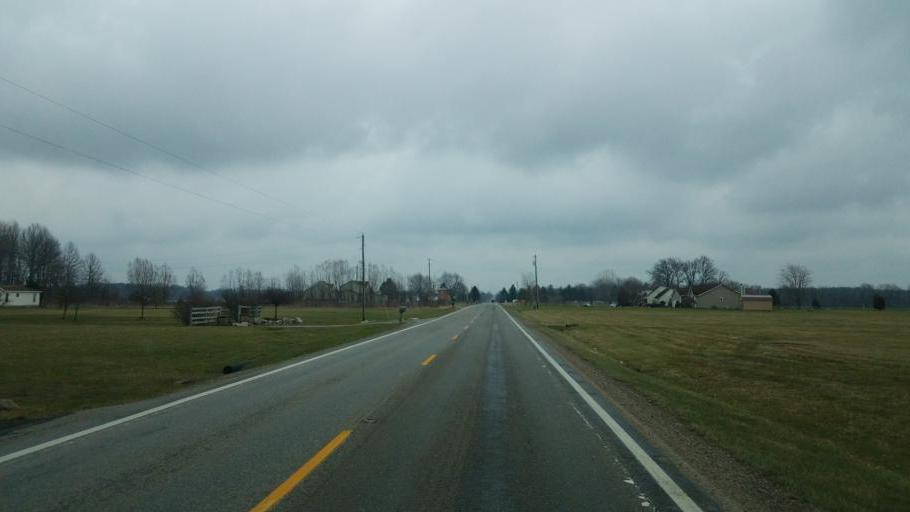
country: US
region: Ohio
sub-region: Delaware County
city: Ashley
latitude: 40.4076
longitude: -82.9199
